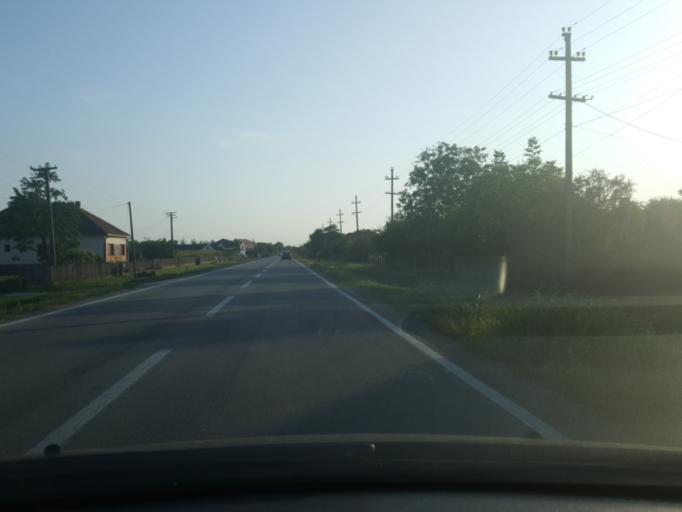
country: RS
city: Lipolist
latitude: 44.7383
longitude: 19.5201
